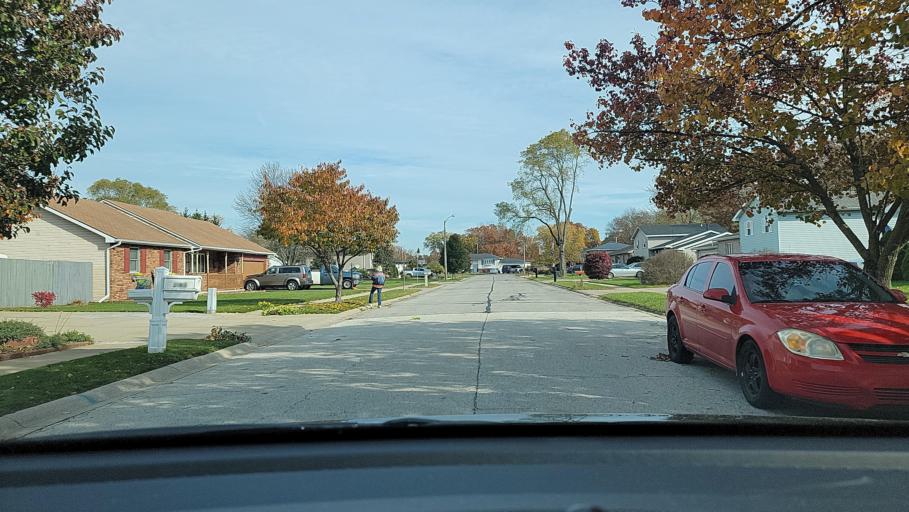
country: US
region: Indiana
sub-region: Lake County
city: Lake Station
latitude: 41.5819
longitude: -87.2151
